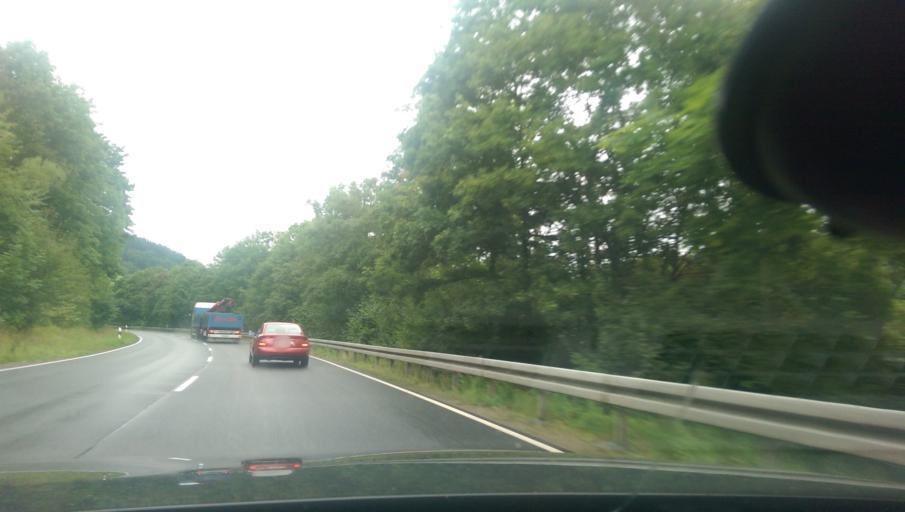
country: DE
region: Hesse
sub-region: Regierungsbezirk Kassel
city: Grossalmerode
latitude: 51.2629
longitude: 9.8333
